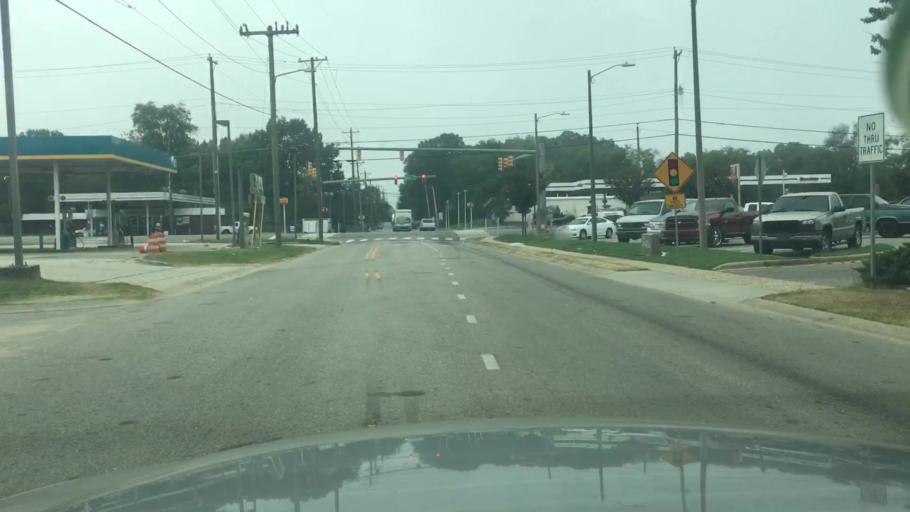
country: US
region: North Carolina
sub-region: Cumberland County
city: Fayetteville
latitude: 35.0539
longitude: -78.8672
